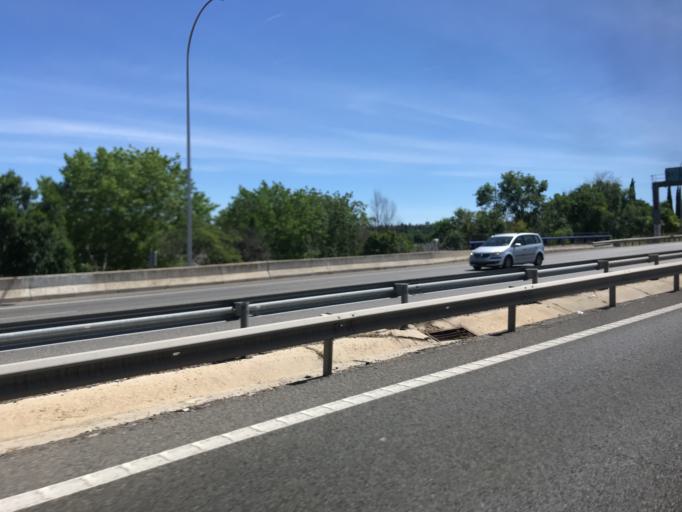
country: ES
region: Madrid
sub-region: Provincia de Madrid
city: Moratalaz
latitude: 40.4154
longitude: -3.6476
